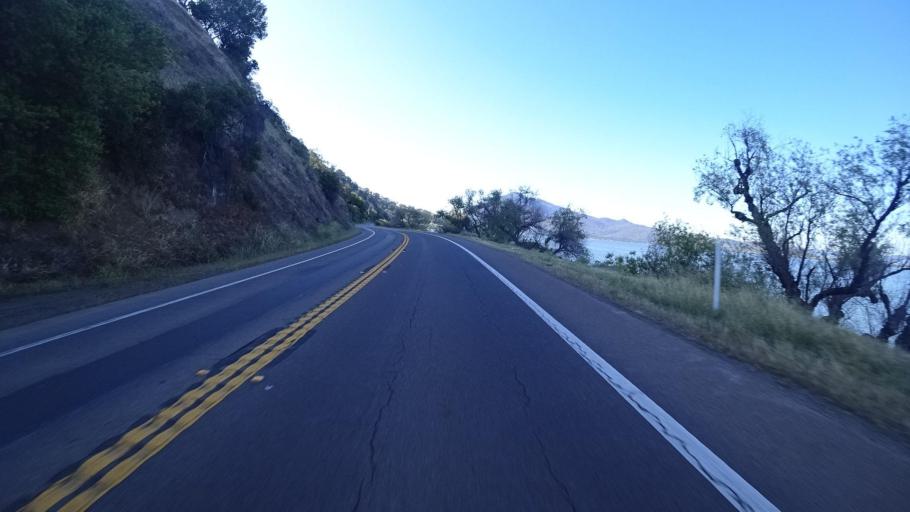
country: US
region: California
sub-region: Lake County
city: Lucerne
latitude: 39.0545
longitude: -122.7827
